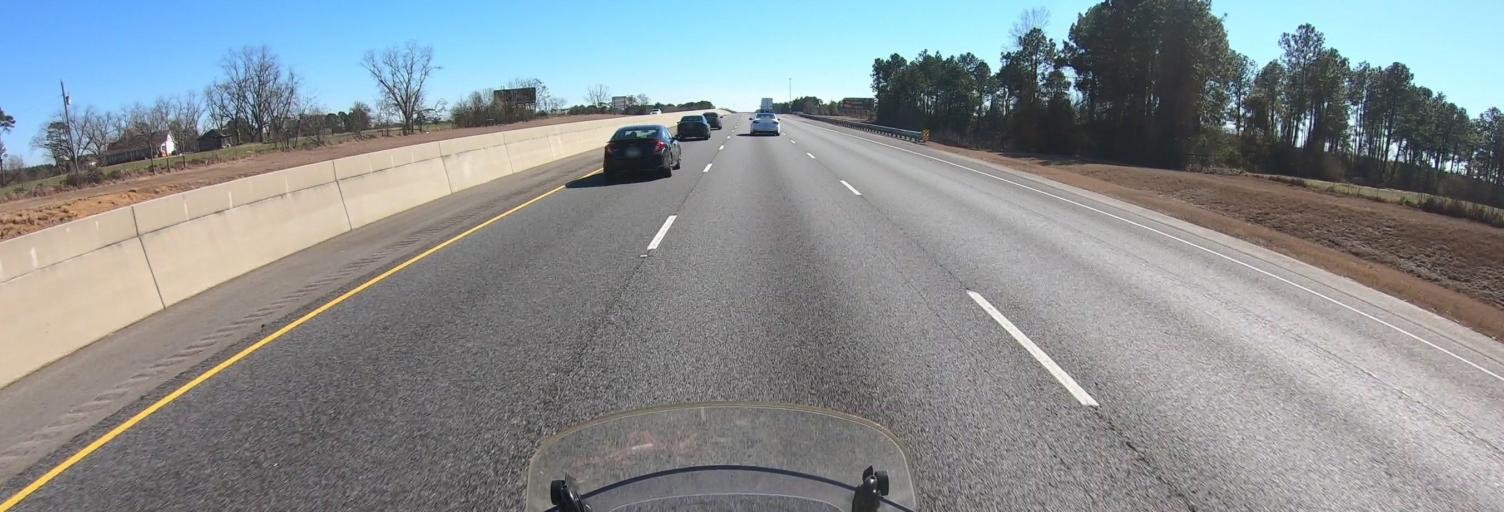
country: US
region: Georgia
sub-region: Turner County
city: Ashburn
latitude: 31.6622
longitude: -83.6036
